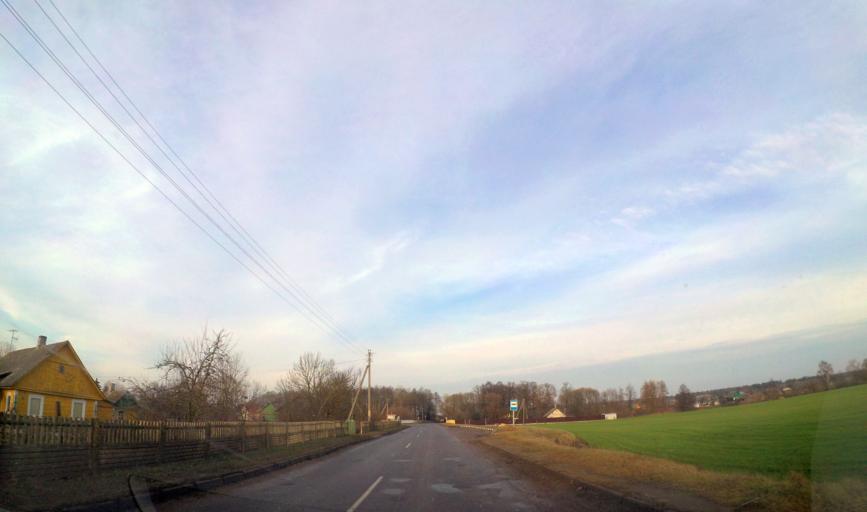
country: BY
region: Grodnenskaya
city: Hrodna
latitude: 53.7579
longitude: 23.9378
